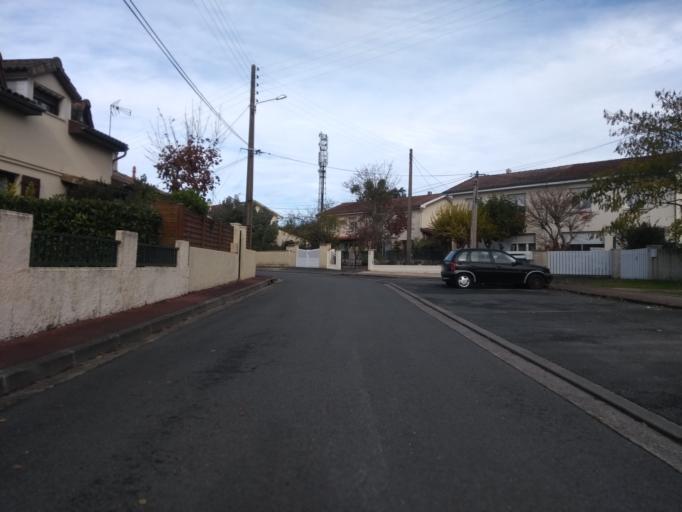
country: FR
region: Aquitaine
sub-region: Departement de la Gironde
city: Gradignan
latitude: 44.7772
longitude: -0.6175
